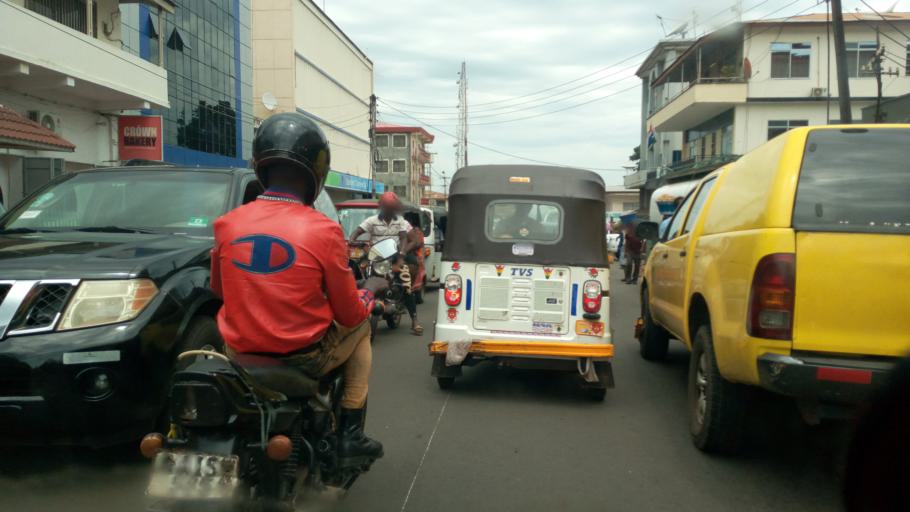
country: SL
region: Western Area
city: Freetown
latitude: 8.4905
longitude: -13.2326
